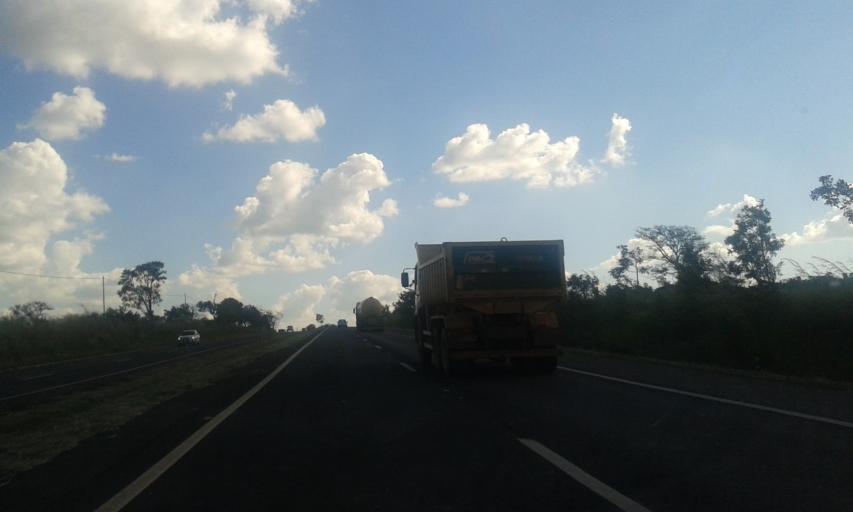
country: BR
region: Minas Gerais
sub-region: Monte Alegre De Minas
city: Monte Alegre de Minas
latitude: -18.8913
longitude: -48.6782
